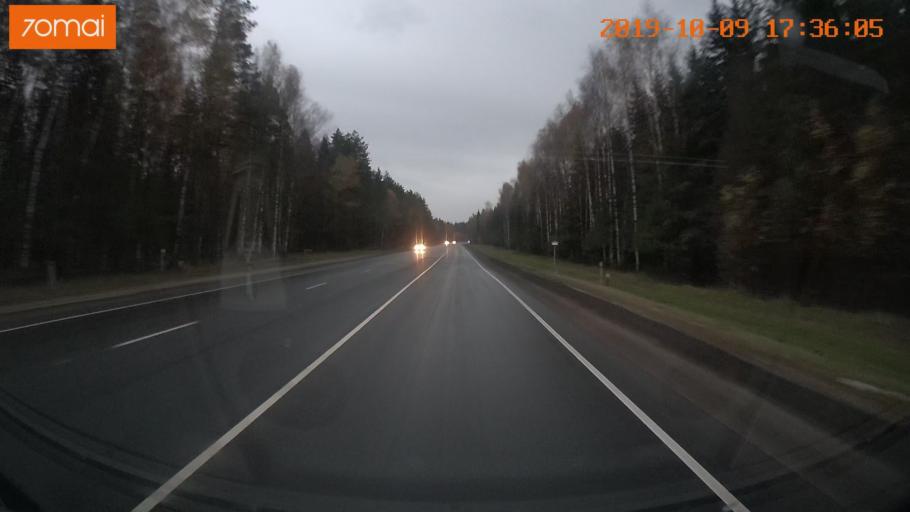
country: RU
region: Ivanovo
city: Bogorodskoye
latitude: 57.0839
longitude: 40.9984
